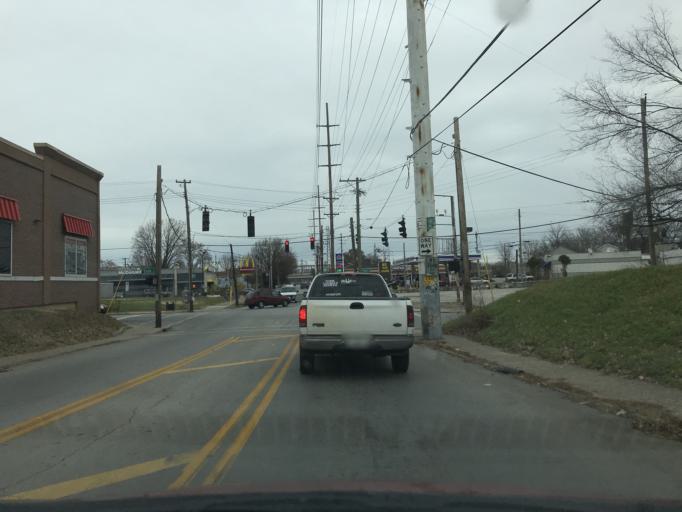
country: US
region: Kentucky
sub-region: Jefferson County
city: Louisville
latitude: 38.2662
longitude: -85.7838
